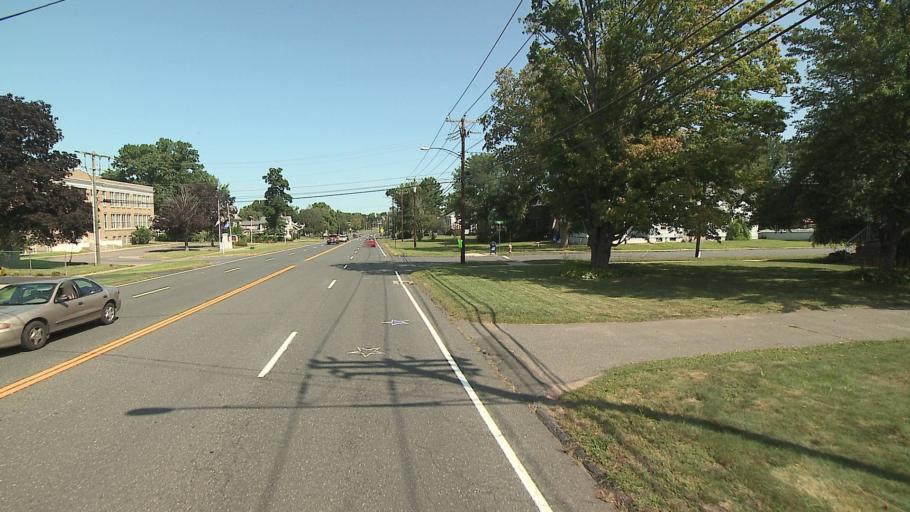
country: US
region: Connecticut
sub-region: Hartford County
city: Thompsonville
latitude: 41.9933
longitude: -72.5941
